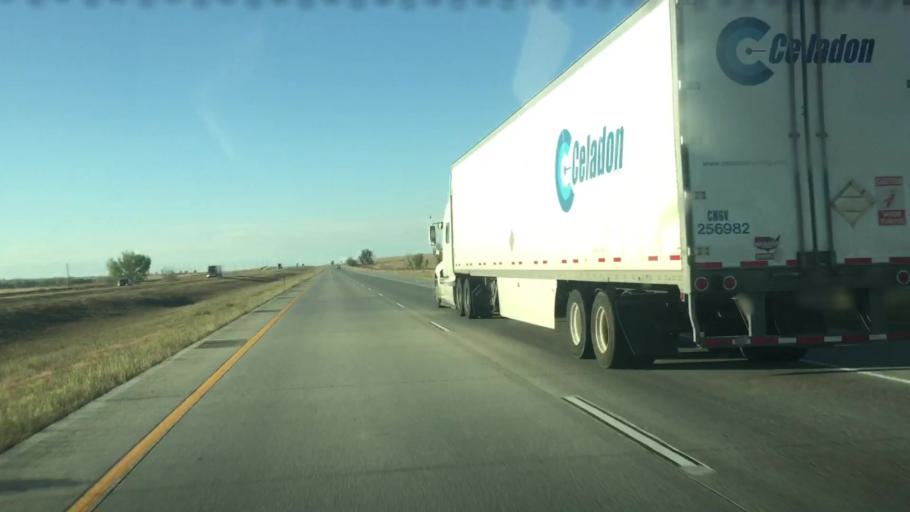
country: US
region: Colorado
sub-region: Arapahoe County
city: Byers
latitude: 39.5683
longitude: -104.0152
